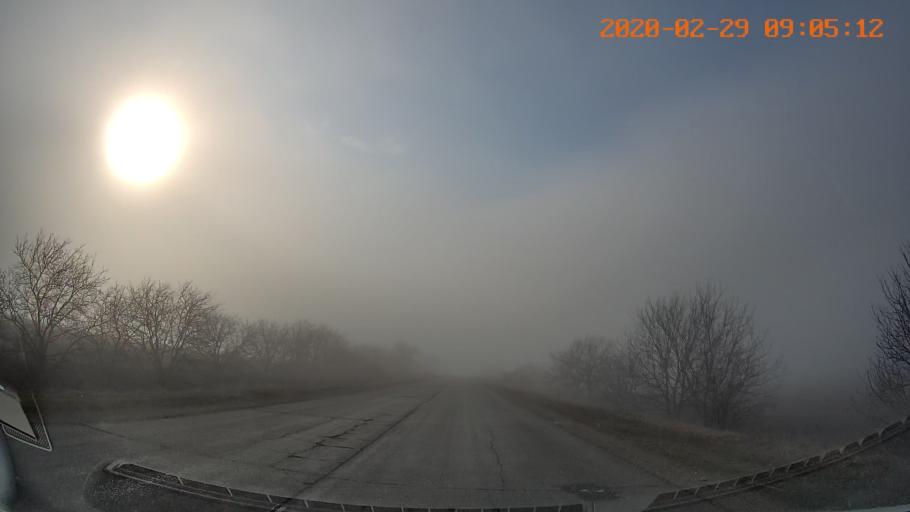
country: MD
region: Telenesti
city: Tiraspolul Nou
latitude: 46.8924
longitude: 29.7392
